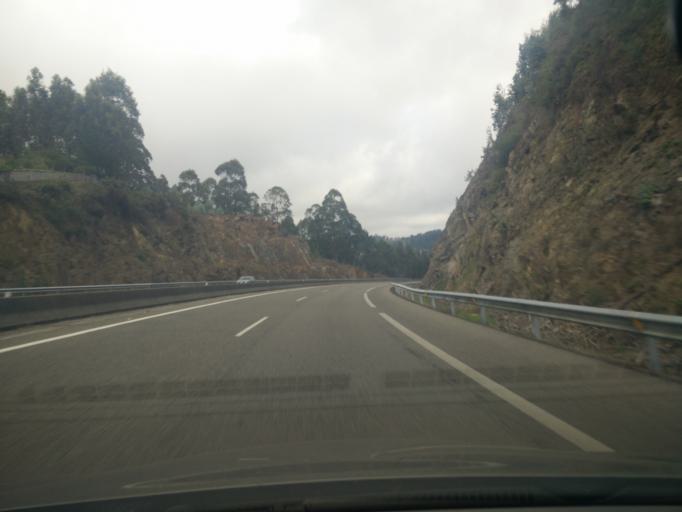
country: ES
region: Galicia
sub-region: Provincia da Coruna
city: Laracha
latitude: 43.2687
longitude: -8.5592
